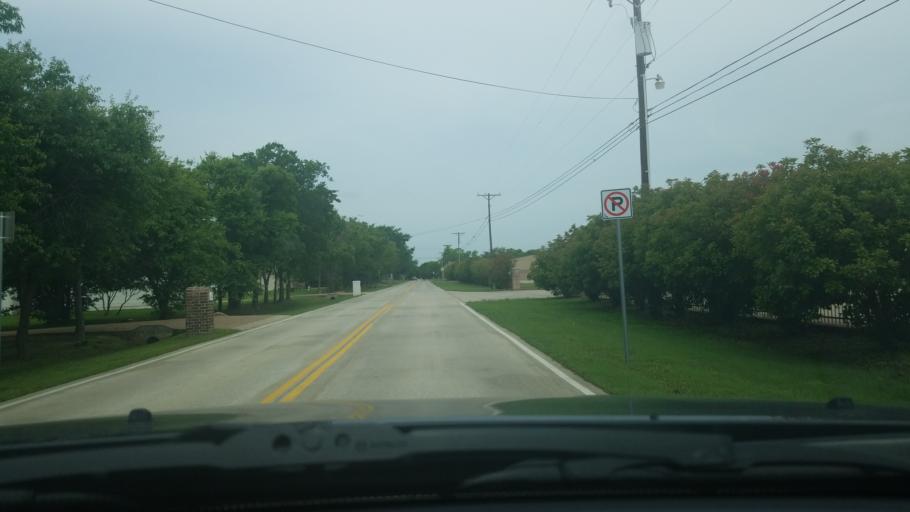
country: US
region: Texas
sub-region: Denton County
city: Lake Dallas
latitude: 33.1087
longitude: -97.0107
